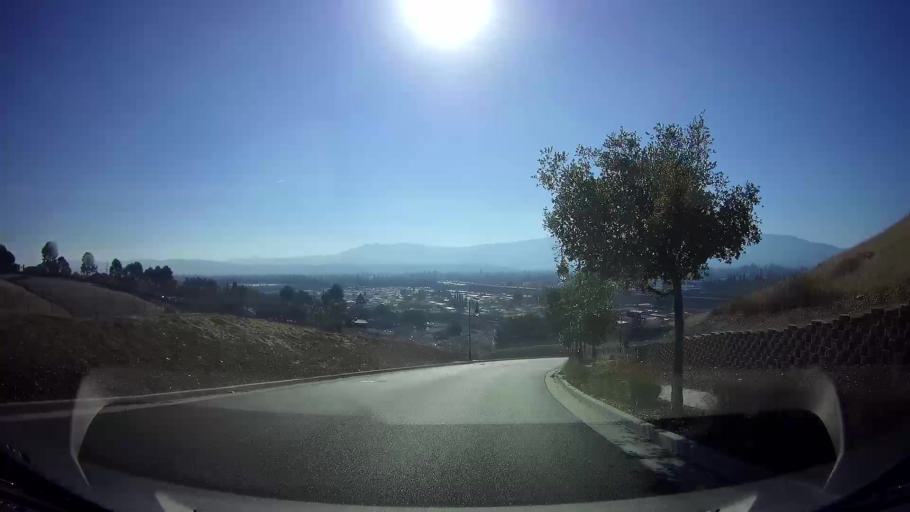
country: US
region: California
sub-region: Santa Clara County
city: Seven Trees
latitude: 37.2845
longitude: -121.8628
